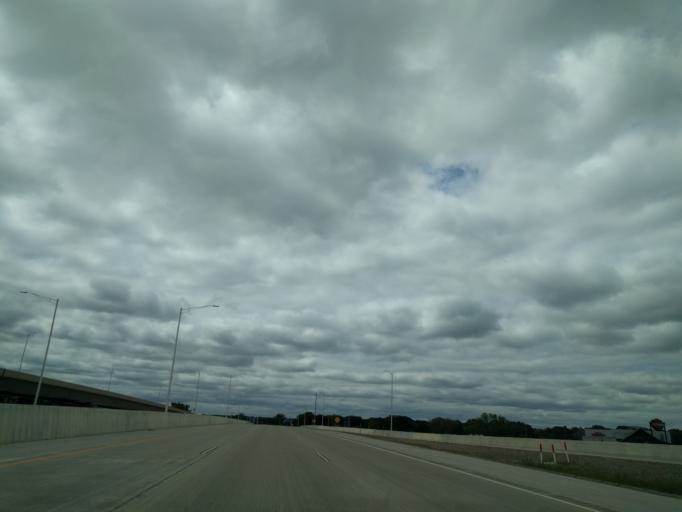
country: US
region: Wisconsin
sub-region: Brown County
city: Howard
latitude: 44.5588
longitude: -88.0575
